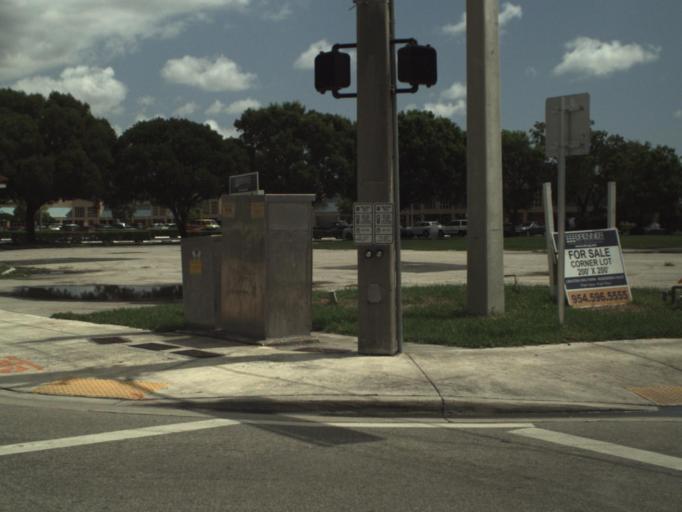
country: US
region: Florida
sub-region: Broward County
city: Margate
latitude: 26.2446
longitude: -80.2013
